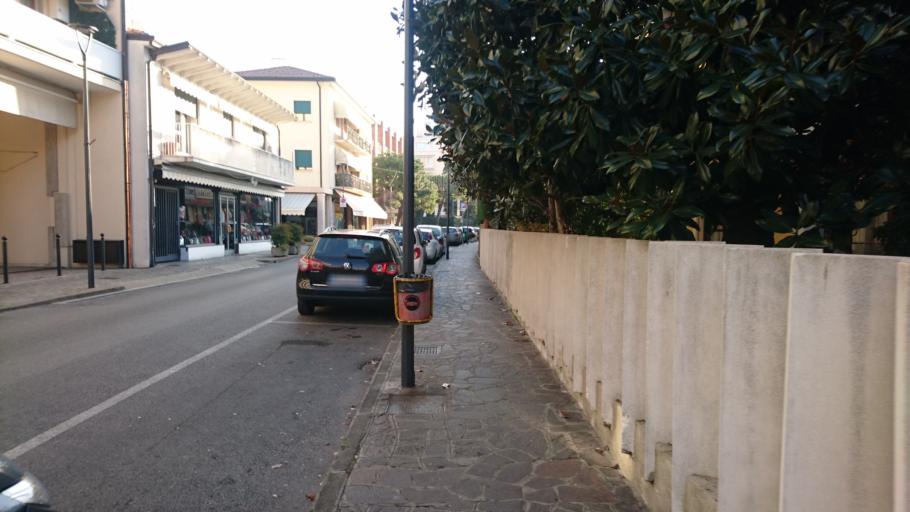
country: IT
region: Veneto
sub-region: Provincia di Padova
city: Abano Terme
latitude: 45.3511
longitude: 11.7790
